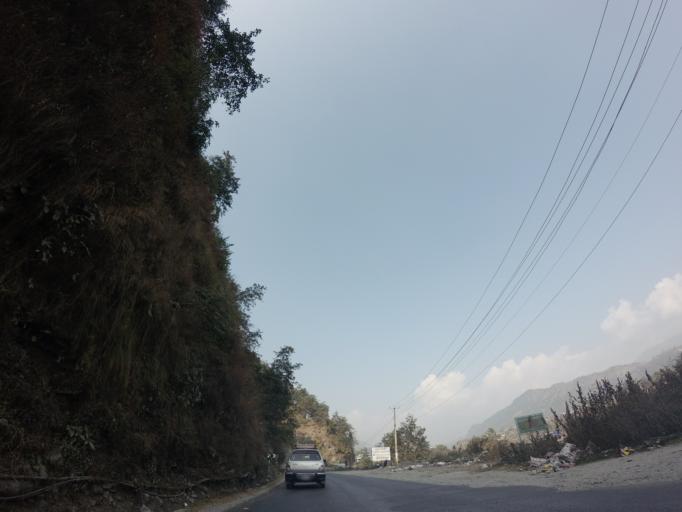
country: NP
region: Western Region
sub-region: Gandaki Zone
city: Pokhara
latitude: 28.2523
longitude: 83.9670
